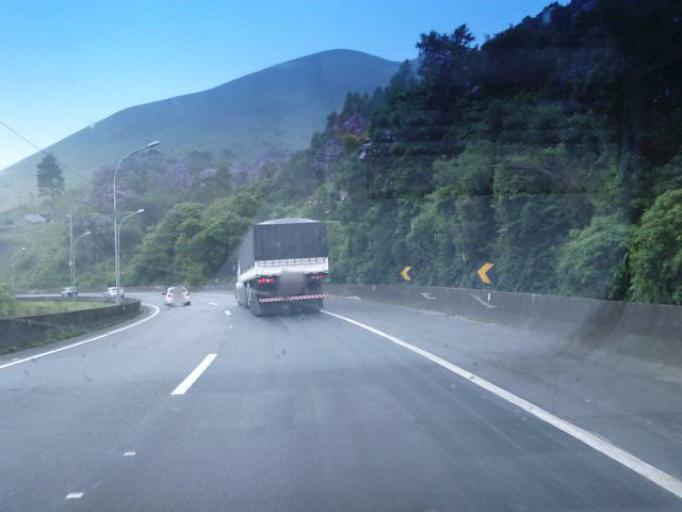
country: BR
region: Parana
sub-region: Campina Grande Do Sul
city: Campina Grande do Sul
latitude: -25.1112
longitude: -48.8161
